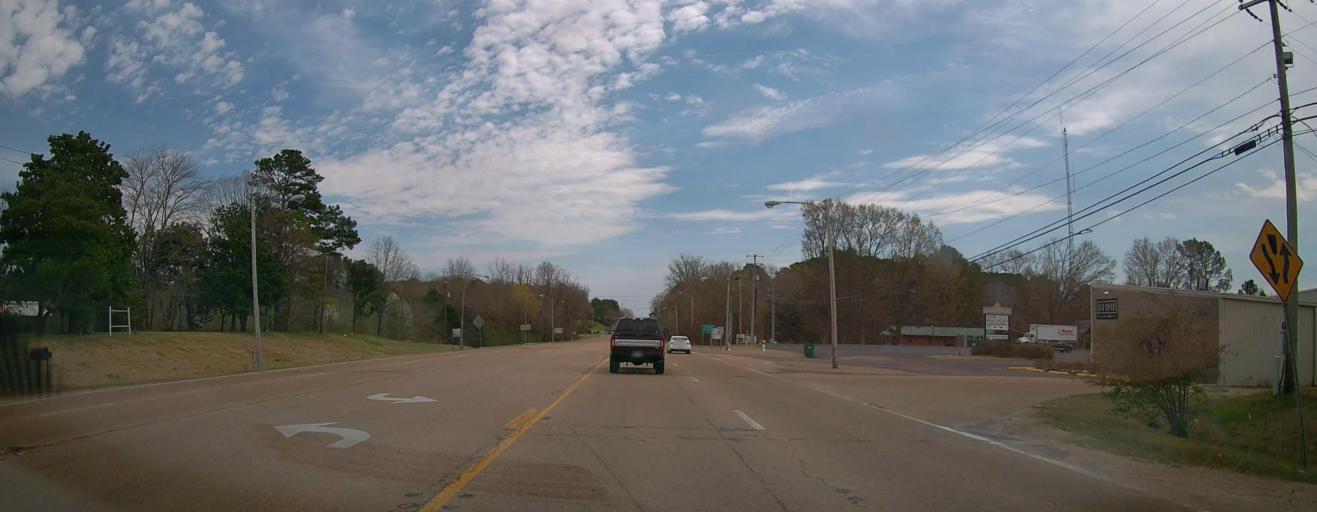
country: US
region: Mississippi
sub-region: Lee County
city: Tupelo
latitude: 34.2845
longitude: -88.7371
